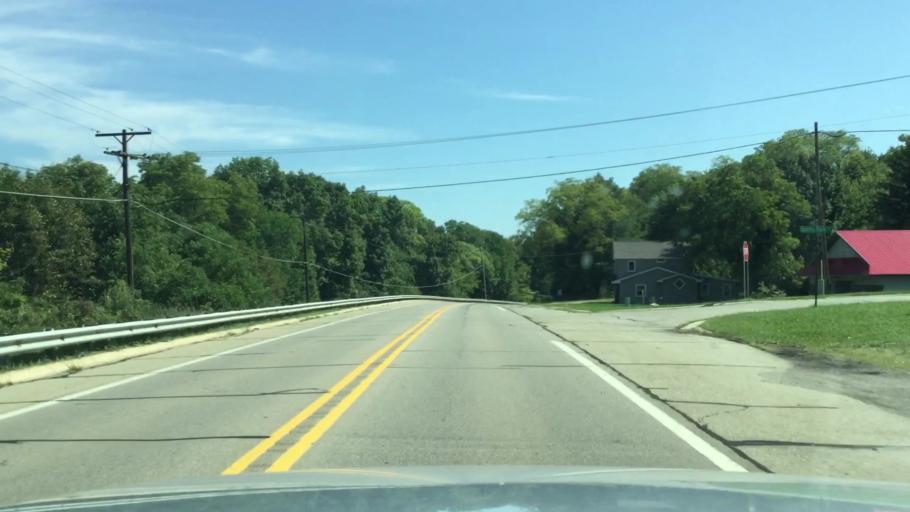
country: US
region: Michigan
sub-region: Jackson County
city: Brooklyn
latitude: 42.0567
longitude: -84.1553
